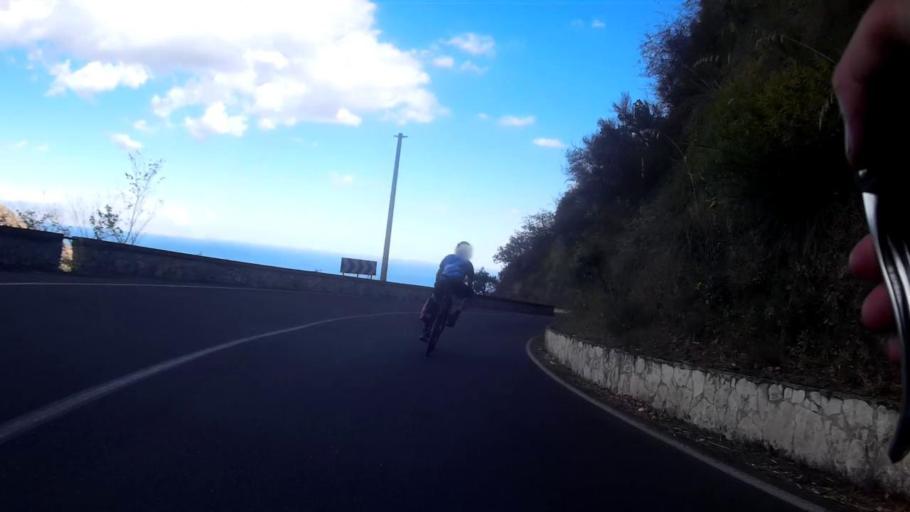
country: IT
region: Sicily
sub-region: Messina
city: Castelmola
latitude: 37.8634
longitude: 15.2773
